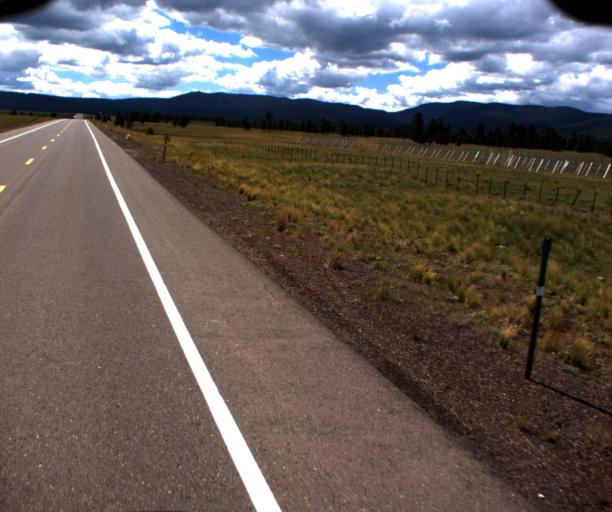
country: US
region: Arizona
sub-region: Apache County
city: Eagar
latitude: 34.0366
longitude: -109.5880
